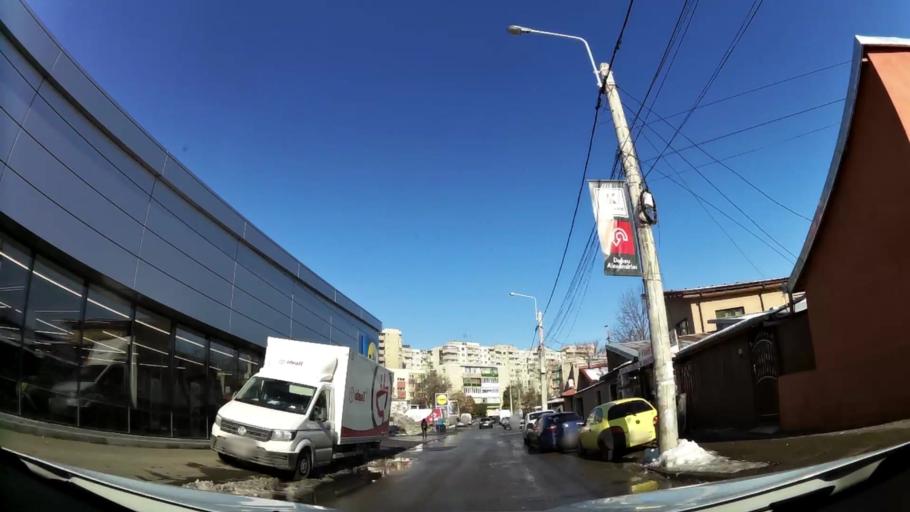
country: RO
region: Bucuresti
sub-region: Municipiul Bucuresti
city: Bucuresti
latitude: 44.4014
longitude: 26.0564
